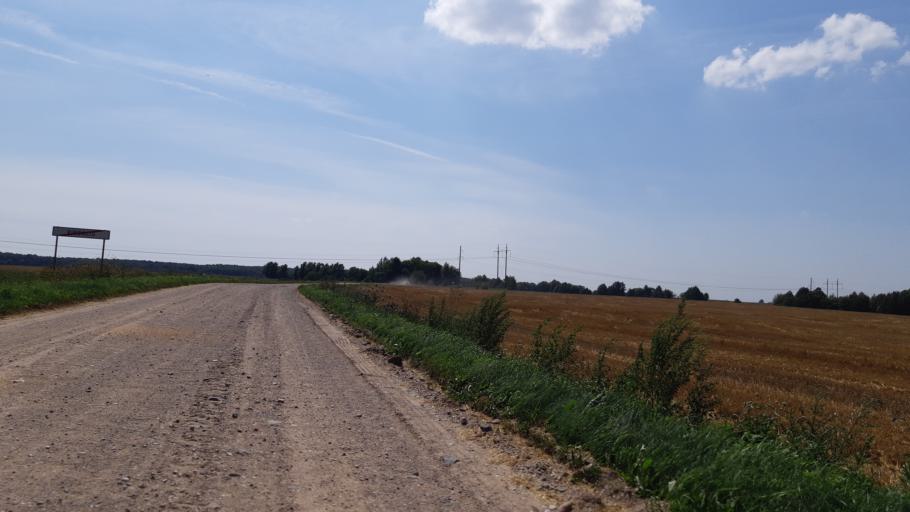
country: LT
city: Virbalis
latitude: 54.6217
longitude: 22.8080
